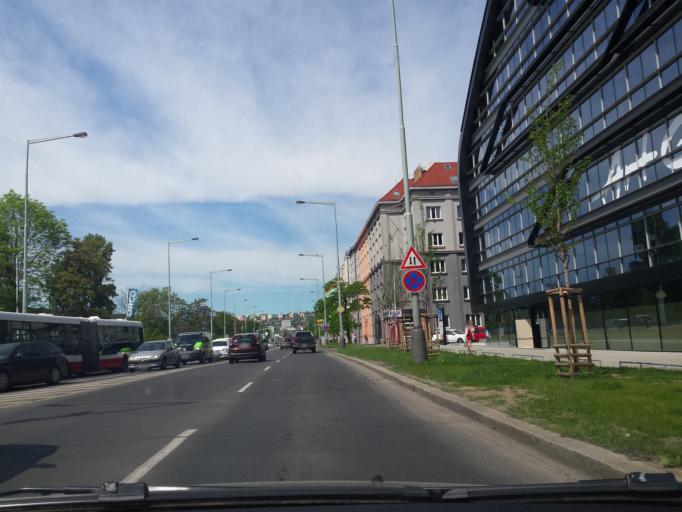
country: CZ
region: Praha
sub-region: Praha 8
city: Karlin
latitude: 50.1012
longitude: 14.4433
